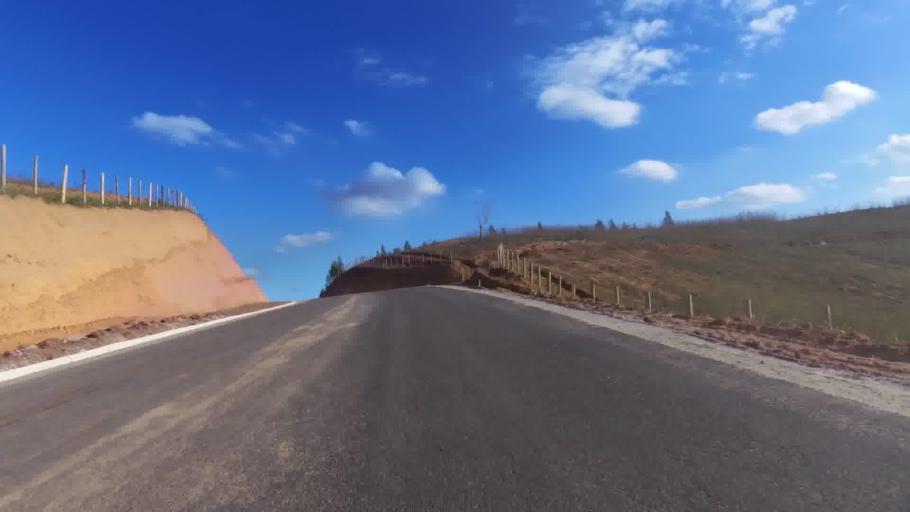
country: BR
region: Espirito Santo
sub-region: Marataizes
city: Marataizes
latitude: -21.1237
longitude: -41.0499
